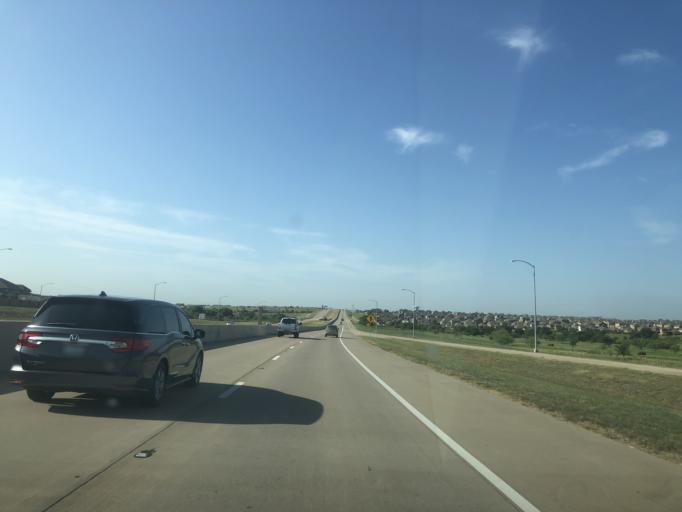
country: US
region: Texas
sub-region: Tarrant County
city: Benbrook
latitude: 32.6270
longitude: -97.4127
